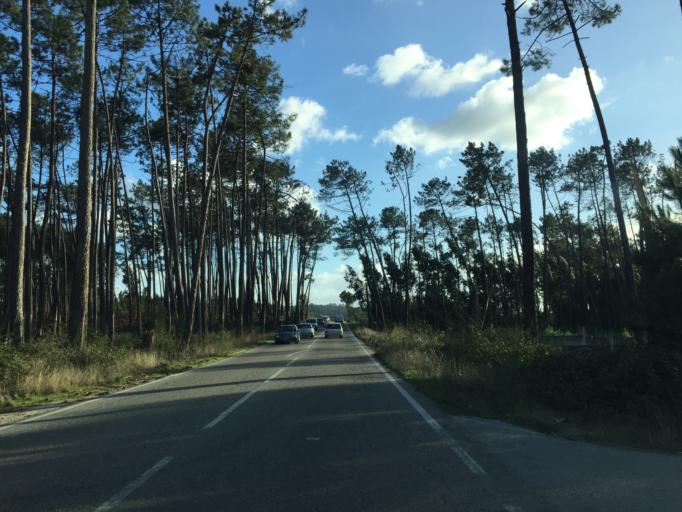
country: PT
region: Leiria
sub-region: Leiria
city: Monte Redondo
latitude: 39.8752
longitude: -8.8387
